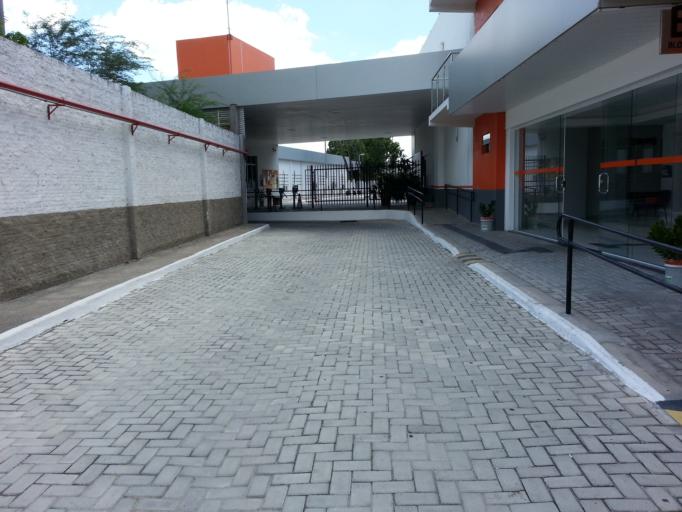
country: BR
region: Ceara
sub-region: Quixada
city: Quixada
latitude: -4.9749
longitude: -39.0143
